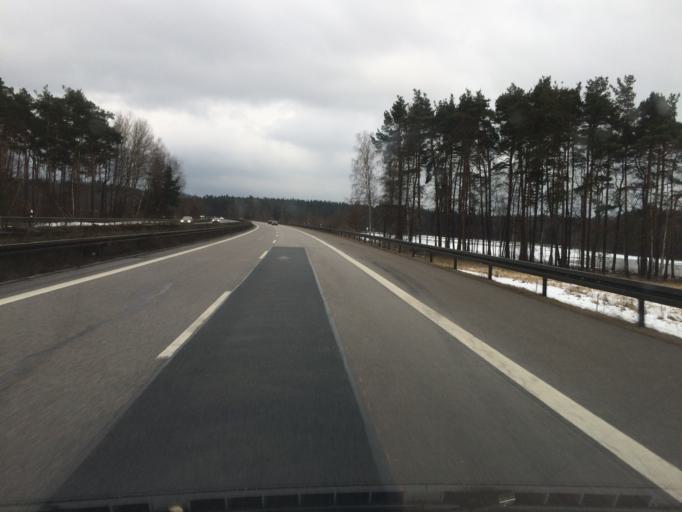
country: DE
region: Bavaria
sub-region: Upper Palatinate
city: Teublitz
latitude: 49.2610
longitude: 12.1223
